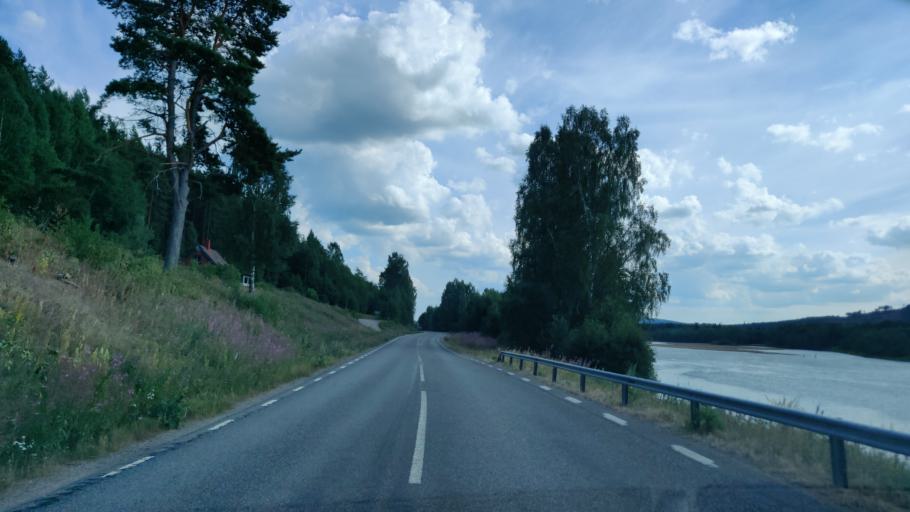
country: SE
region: Vaermland
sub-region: Hagfors Kommun
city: Ekshaerad
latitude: 60.1697
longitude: 13.5297
